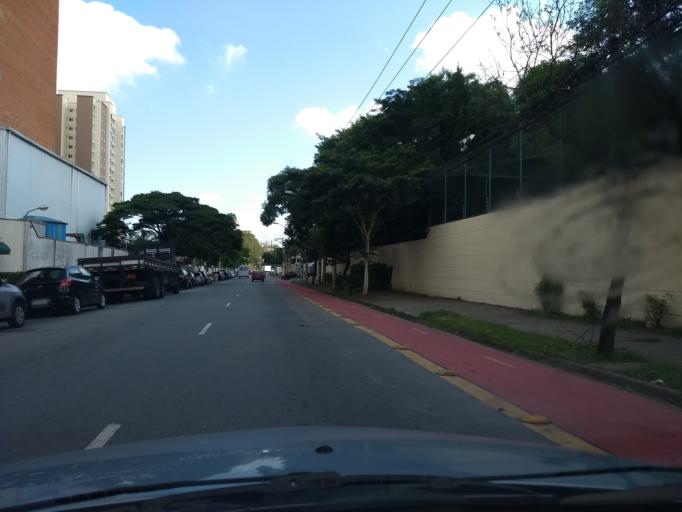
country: BR
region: Sao Paulo
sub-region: Osasco
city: Osasco
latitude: -23.5516
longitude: -46.7437
